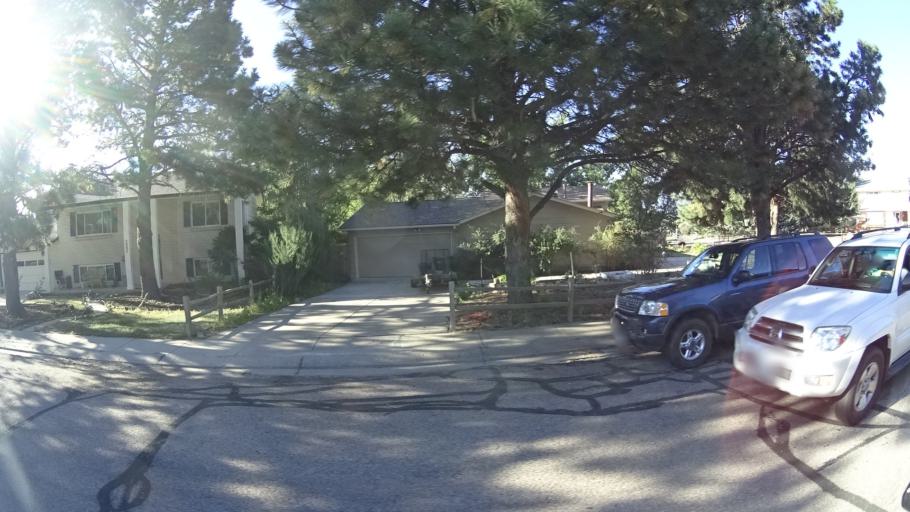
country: US
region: Colorado
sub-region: El Paso County
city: Cimarron Hills
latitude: 38.9086
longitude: -104.7558
